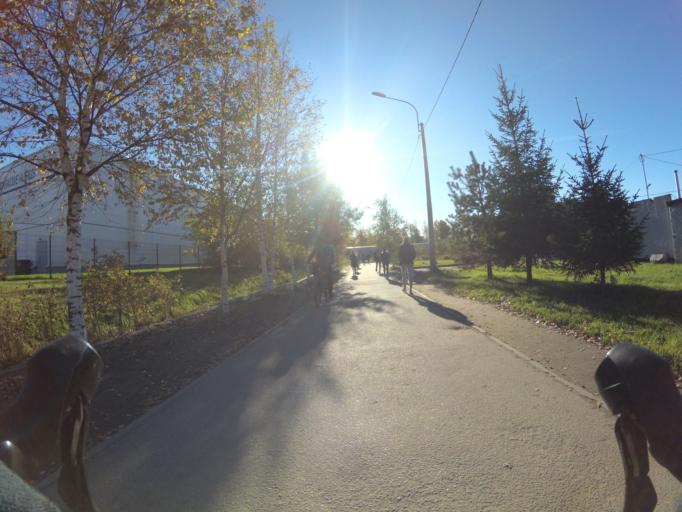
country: RU
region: Leningrad
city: Untolovo
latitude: 59.9945
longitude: 30.2040
